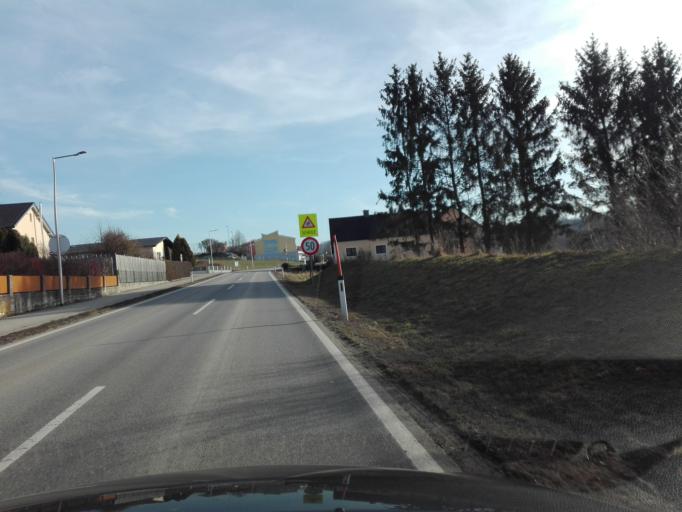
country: AT
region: Lower Austria
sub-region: Politischer Bezirk Amstetten
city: Amstetten
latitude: 48.1700
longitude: 14.8382
